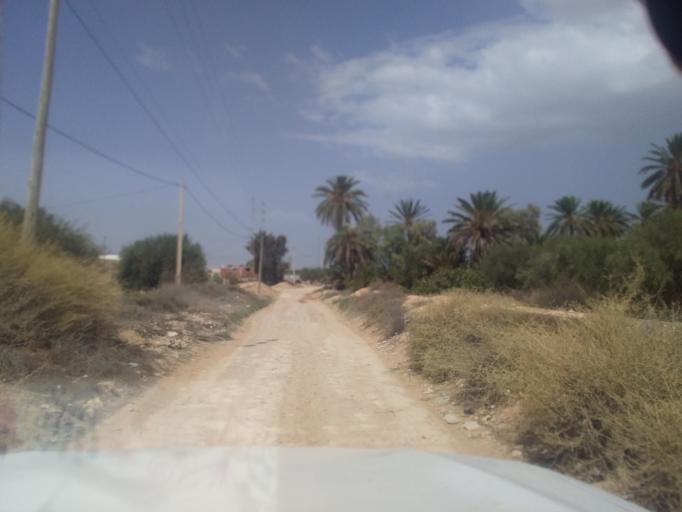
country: TN
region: Madanin
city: Medenine
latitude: 33.5927
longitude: 10.3264
